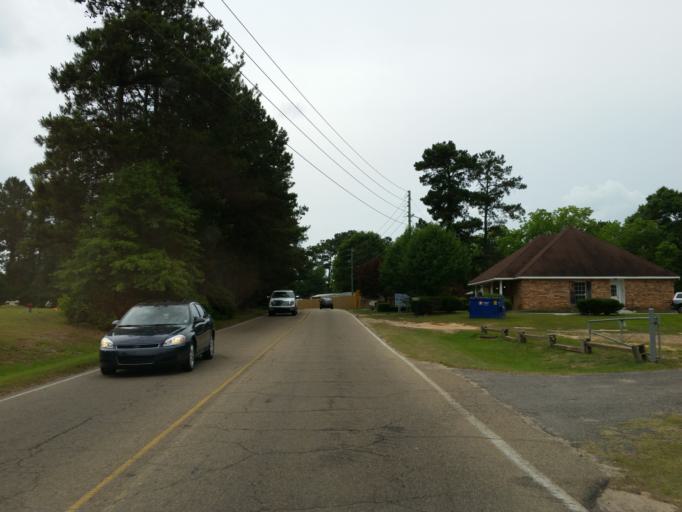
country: US
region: Mississippi
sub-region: Lamar County
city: West Hattiesburg
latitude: 31.3044
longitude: -89.3749
